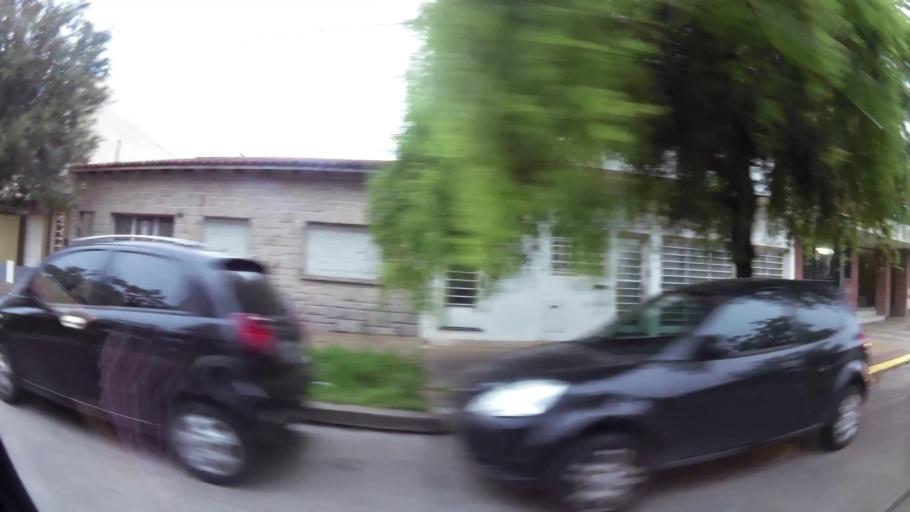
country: AR
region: Buenos Aires
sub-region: Partido de La Plata
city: La Plata
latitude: -34.9144
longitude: -57.9715
